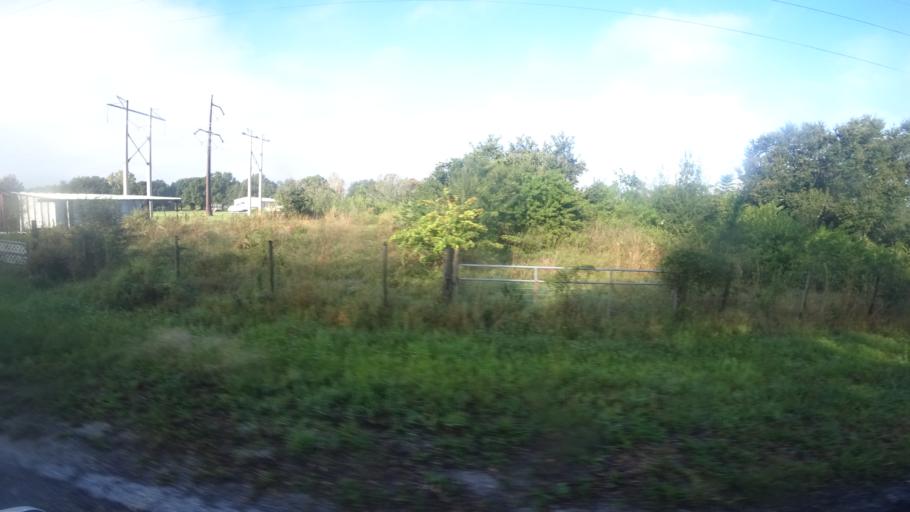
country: US
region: Florida
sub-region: Manatee County
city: Ellenton
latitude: 27.5382
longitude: -82.4582
